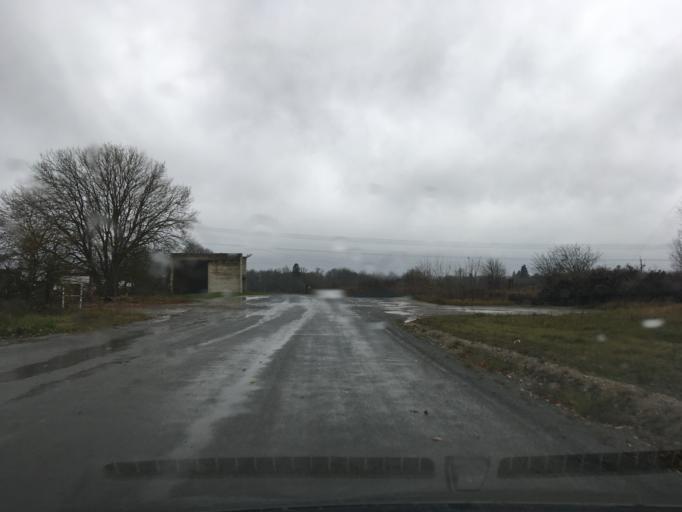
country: EE
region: Laeaene
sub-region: Lihula vald
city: Lihula
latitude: 58.6760
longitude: 23.8221
